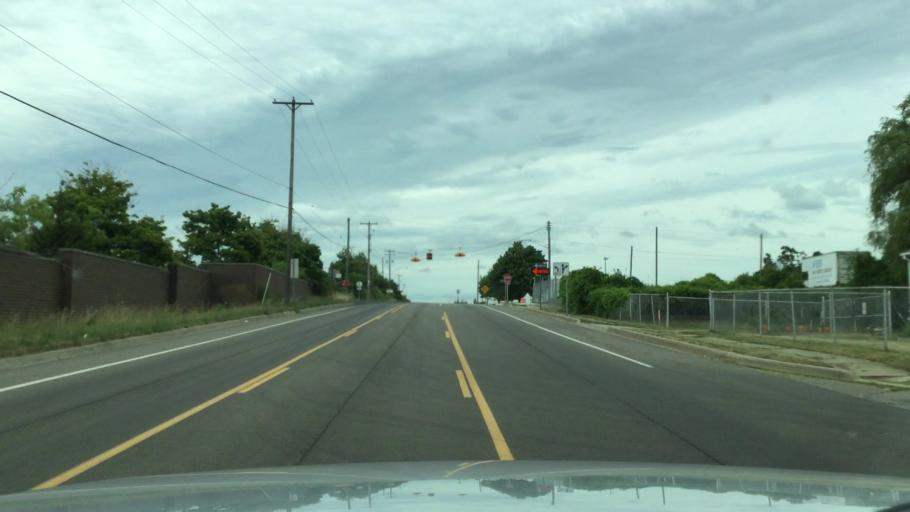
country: US
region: Michigan
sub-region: Genesee County
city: Beecher
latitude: 43.0894
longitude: -83.6860
